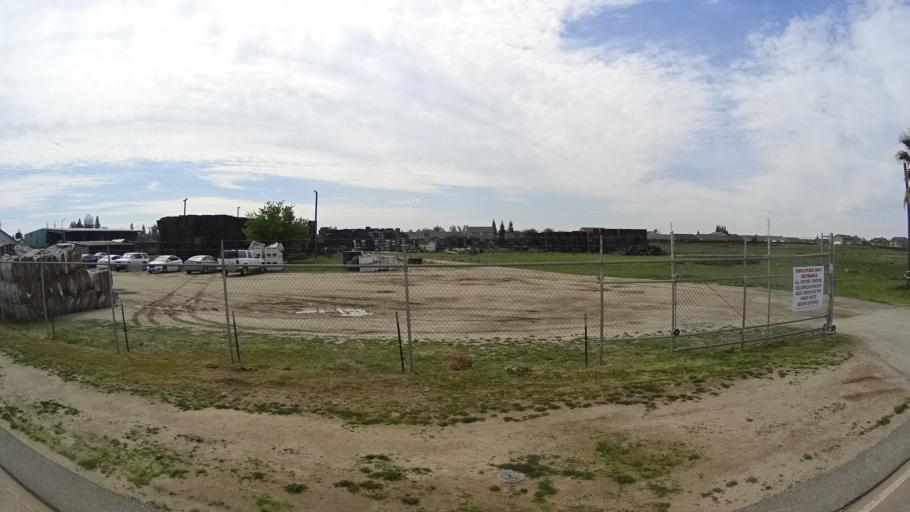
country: US
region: California
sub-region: Fresno County
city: West Park
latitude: 36.7863
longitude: -119.8914
